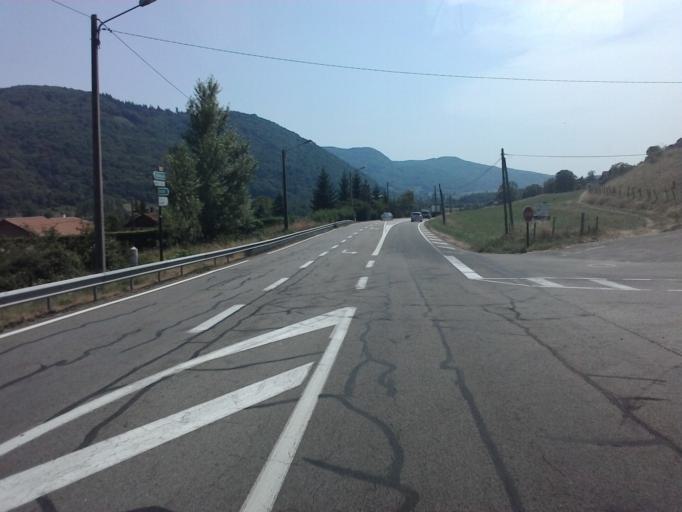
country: FR
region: Rhone-Alpes
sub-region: Departement de l'Isere
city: Chirens
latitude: 45.4322
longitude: 5.5661
